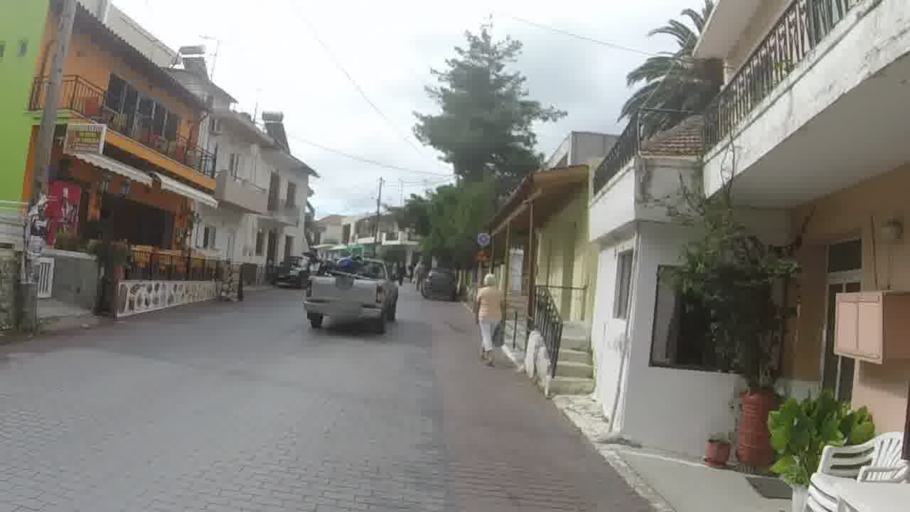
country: GR
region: Crete
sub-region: Nomos Rethymnis
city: Agia Foteini
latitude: 35.2173
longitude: 24.5358
